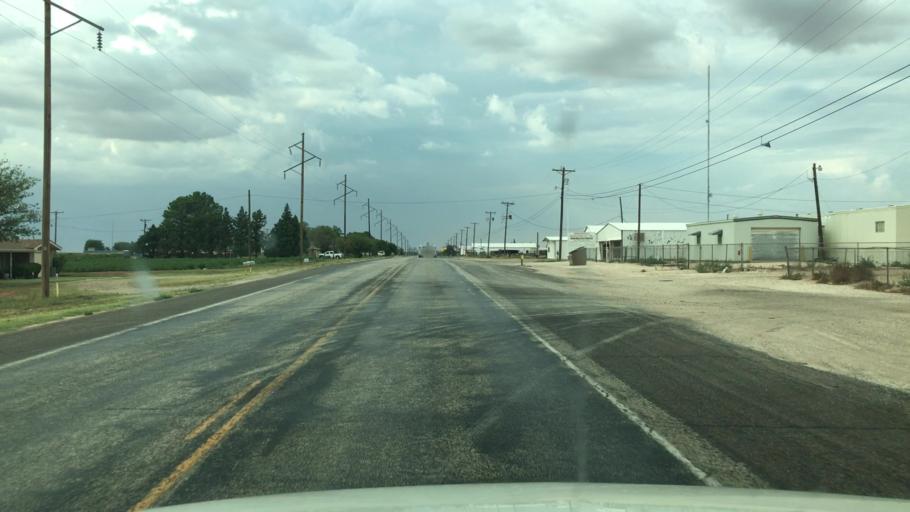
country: US
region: Texas
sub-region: Terry County
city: Brownfield
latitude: 33.1694
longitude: -102.2915
